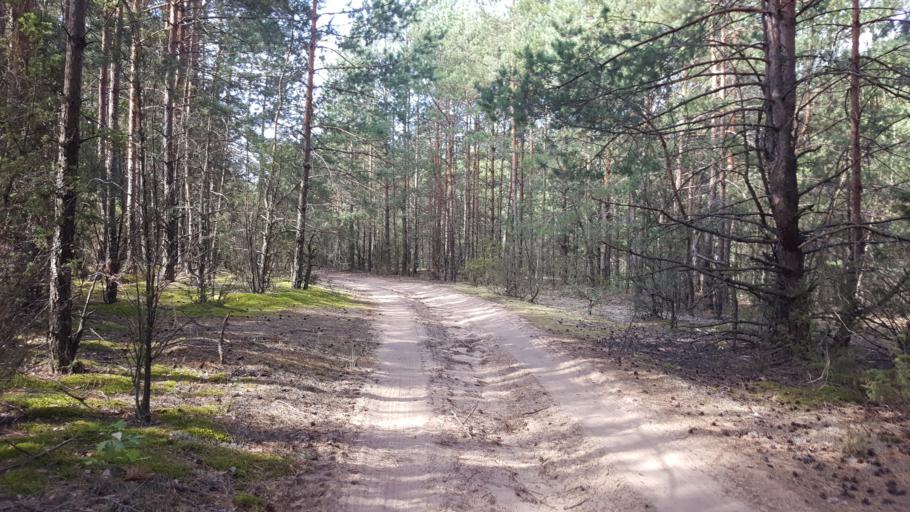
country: BY
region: Brest
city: Ivatsevichy
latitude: 52.7953
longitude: 25.5579
